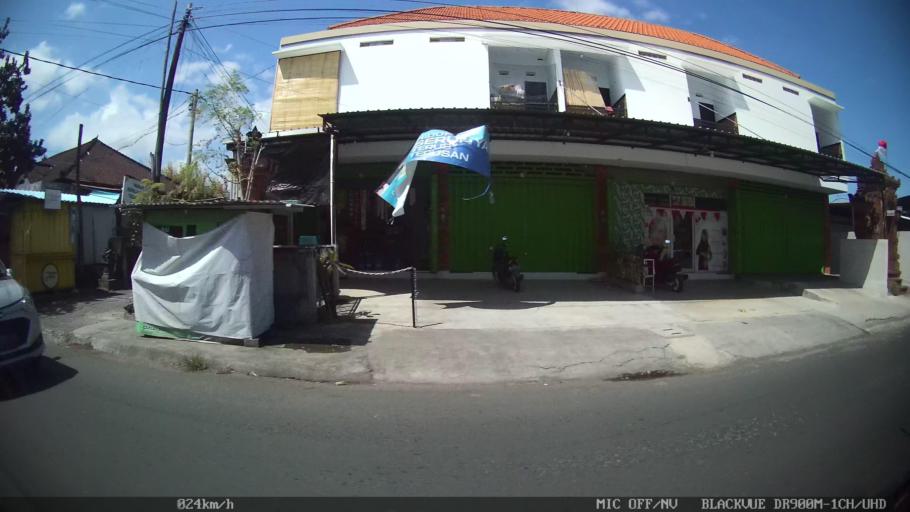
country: ID
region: Bali
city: Denpasar
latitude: -8.6664
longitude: 115.1811
